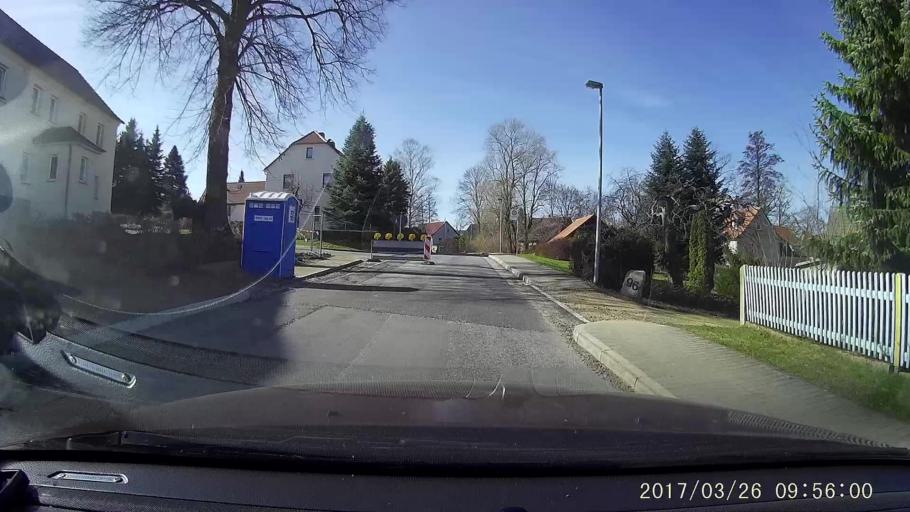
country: DE
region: Saxony
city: Sohland am Rotstein
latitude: 51.0917
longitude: 14.7392
